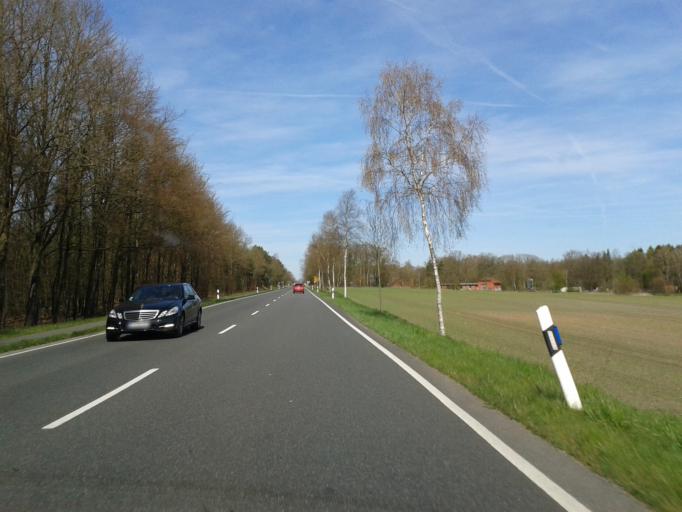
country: DE
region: Lower Saxony
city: Munster
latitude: 52.9706
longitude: 10.1079
